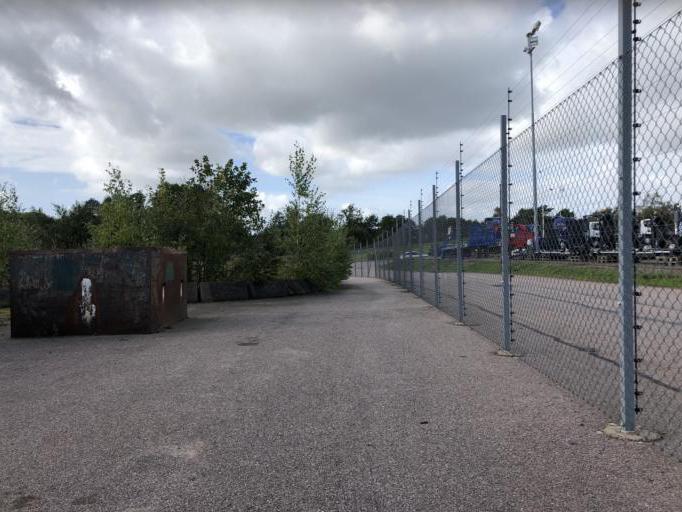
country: SE
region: Vaestra Goetaland
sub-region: Goteborg
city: Majorna
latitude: 57.7506
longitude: 11.8779
